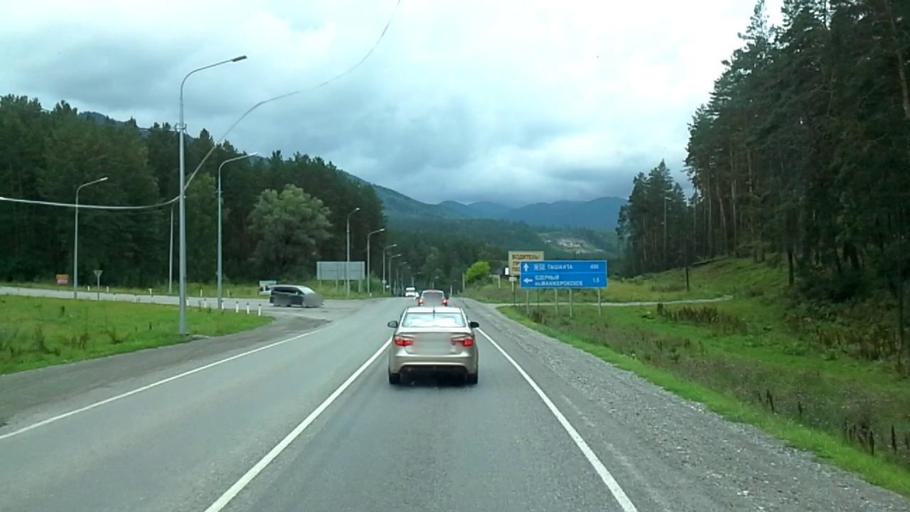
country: RU
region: Altay
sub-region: Mayminskiy Rayon
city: Manzherok
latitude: 51.8218
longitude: 85.7864
